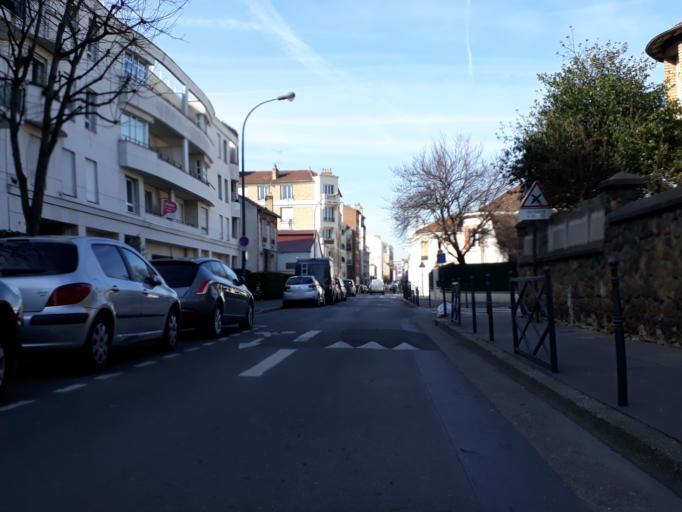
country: FR
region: Ile-de-France
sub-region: Departement des Hauts-de-Seine
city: Asnieres-sur-Seine
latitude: 48.9187
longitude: 2.2866
